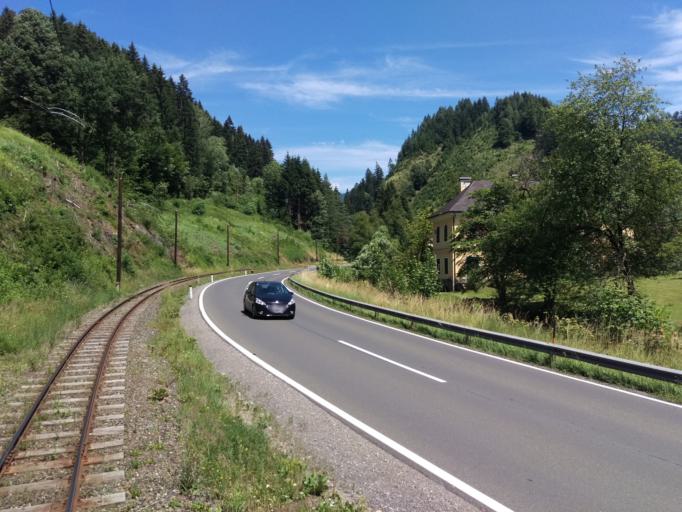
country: AT
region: Styria
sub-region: Politischer Bezirk Bruck-Muerzzuschlag
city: Pernegg an der Mur
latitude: 47.3805
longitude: 15.4010
